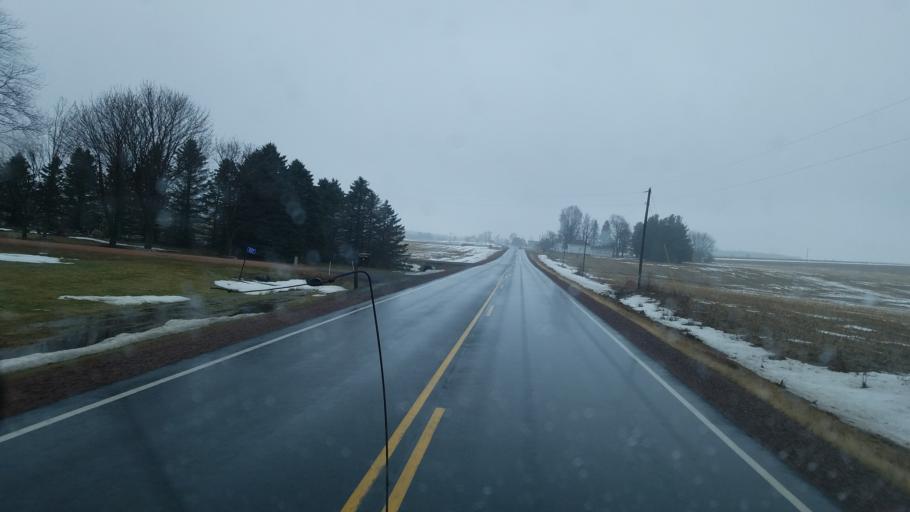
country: US
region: Wisconsin
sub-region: Wood County
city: Marshfield
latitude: 44.5946
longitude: -90.2987
